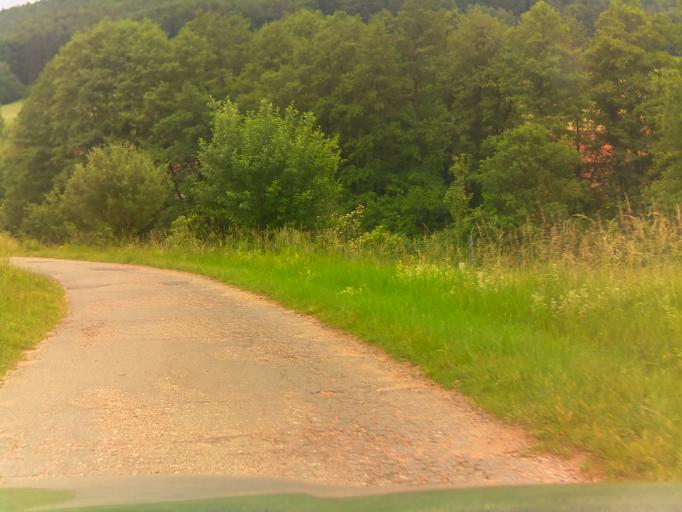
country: DE
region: Bavaria
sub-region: Regierungsbezirk Unterfranken
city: Eschau
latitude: 49.8388
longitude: 9.2769
